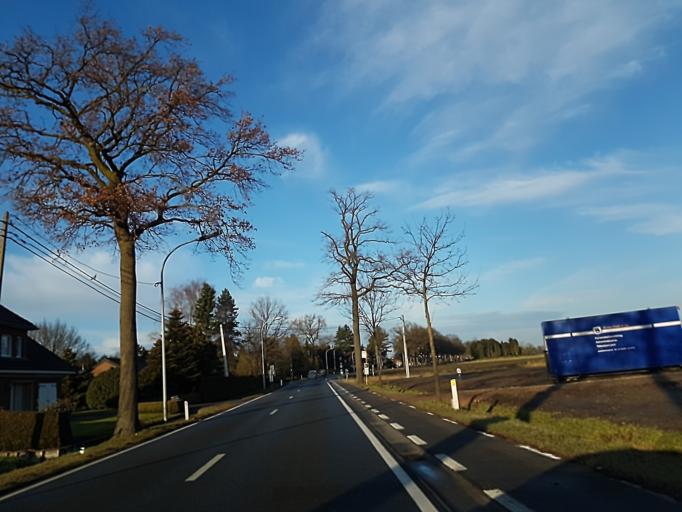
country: BE
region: Flanders
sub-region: Provincie Antwerpen
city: Ravels
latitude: 51.3969
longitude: 4.9994
